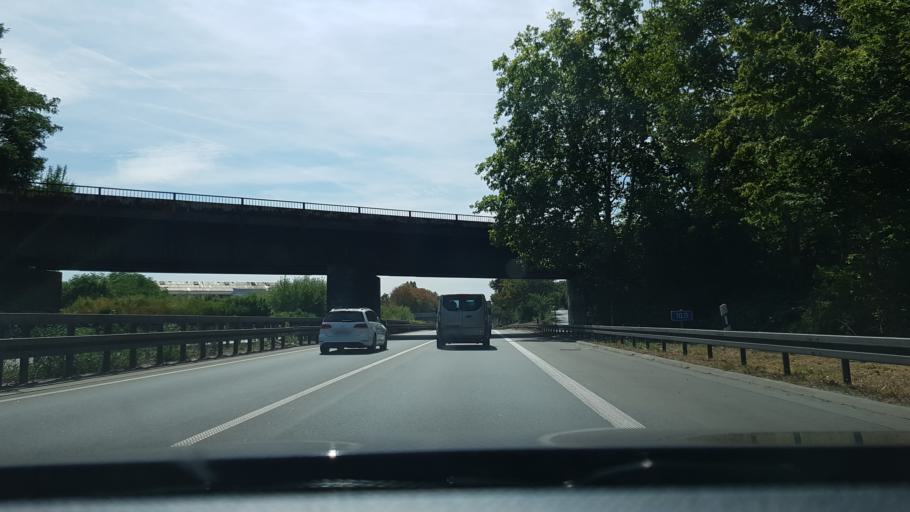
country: DE
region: North Rhine-Westphalia
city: Meiderich
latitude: 51.4781
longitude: 6.7690
